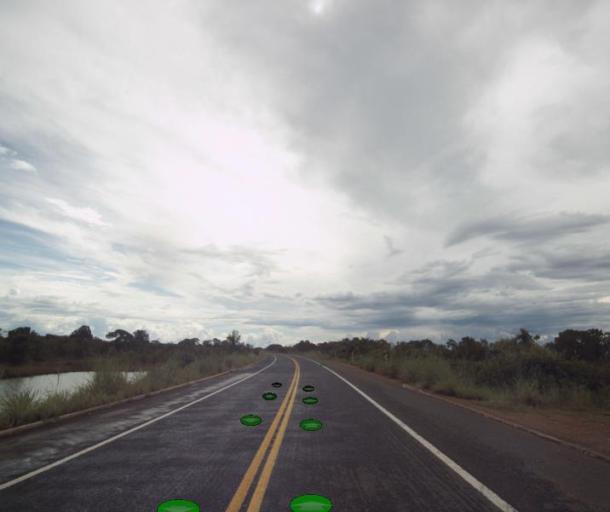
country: BR
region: Goias
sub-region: Sao Miguel Do Araguaia
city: Sao Miguel do Araguaia
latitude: -13.2406
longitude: -50.5410
